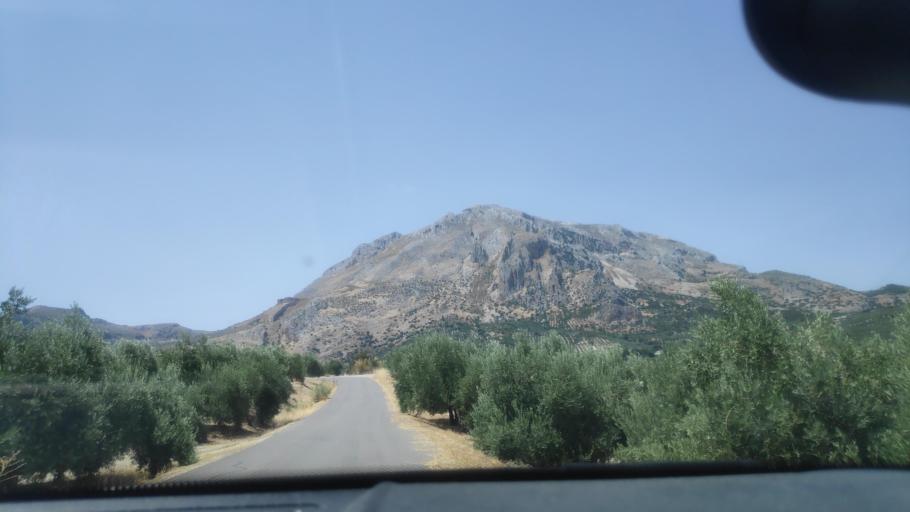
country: ES
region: Andalusia
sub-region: Provincia de Jaen
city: Jimena
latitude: 37.8024
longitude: -3.4440
